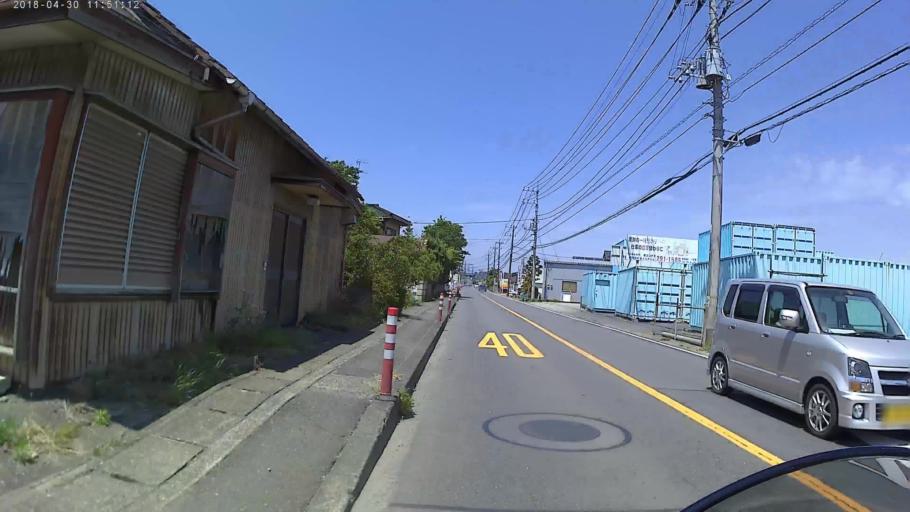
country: JP
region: Kanagawa
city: Zama
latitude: 35.4868
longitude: 139.3477
